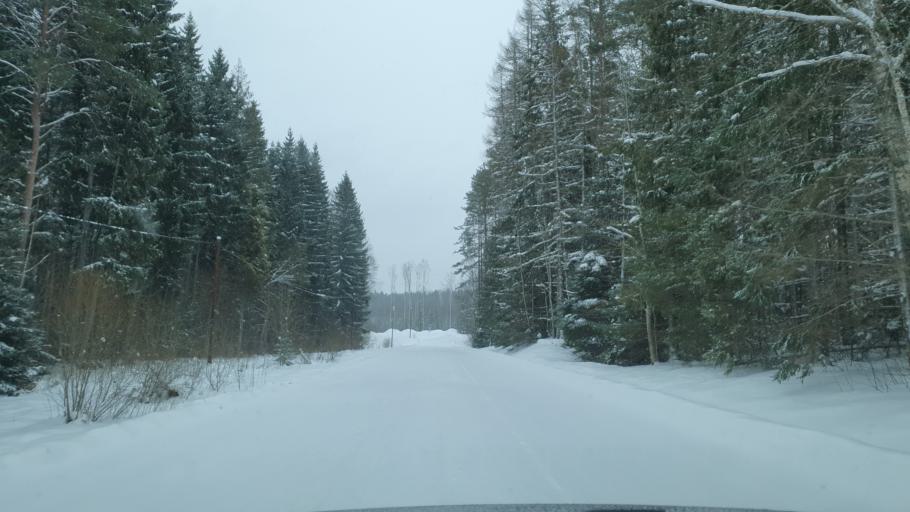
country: EE
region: Tartu
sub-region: Tartu linn
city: Tartu
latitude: 58.5691
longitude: 26.8362
